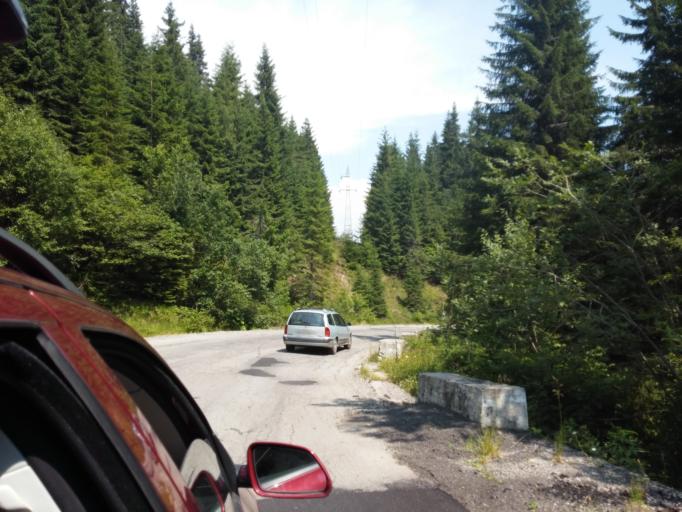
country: RO
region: Valcea
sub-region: Comuna Voineasa
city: Voineasa
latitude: 45.4315
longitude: 23.8048
